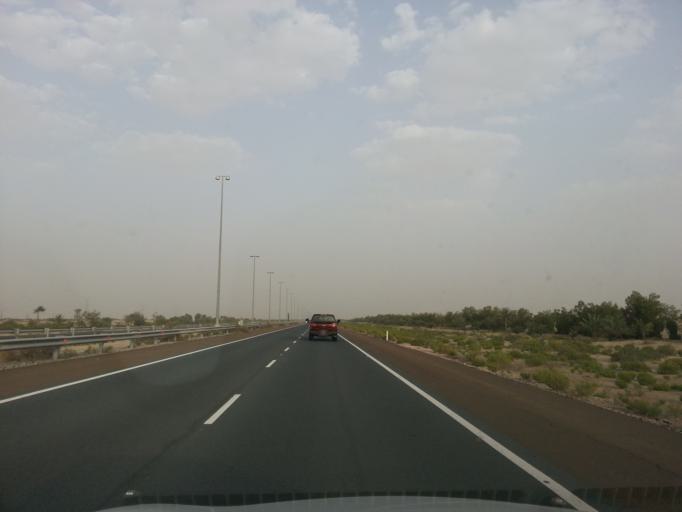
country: AE
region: Dubai
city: Dubai
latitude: 24.5956
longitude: 55.1379
